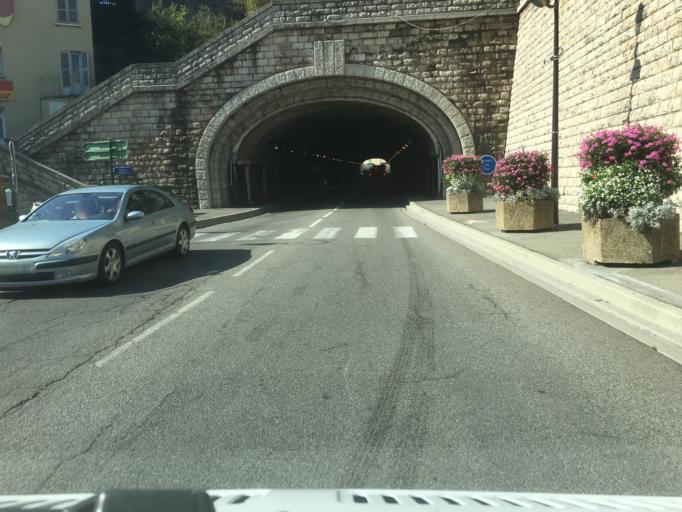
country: FR
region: Provence-Alpes-Cote d'Azur
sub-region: Departement des Alpes-de-Haute-Provence
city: Sisteron
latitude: 44.1990
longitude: 5.9448
